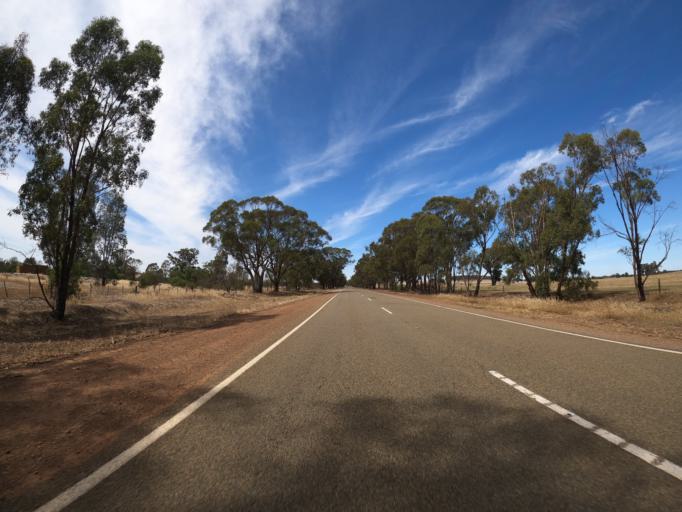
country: AU
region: Victoria
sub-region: Benalla
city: Benalla
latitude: -36.3093
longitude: 145.9583
